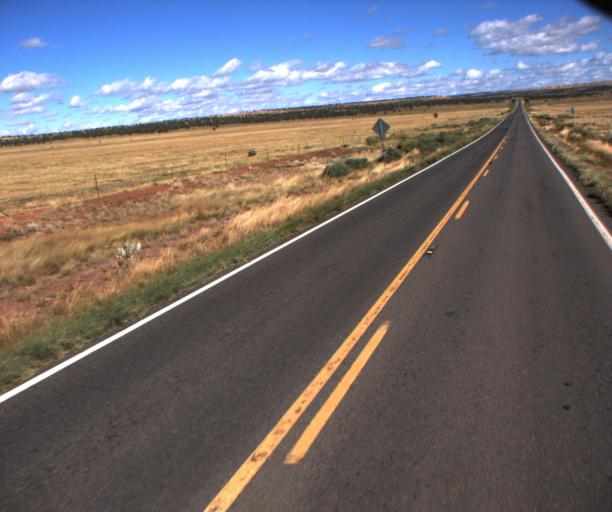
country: US
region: Arizona
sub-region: Apache County
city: Saint Johns
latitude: 34.7592
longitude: -109.2427
